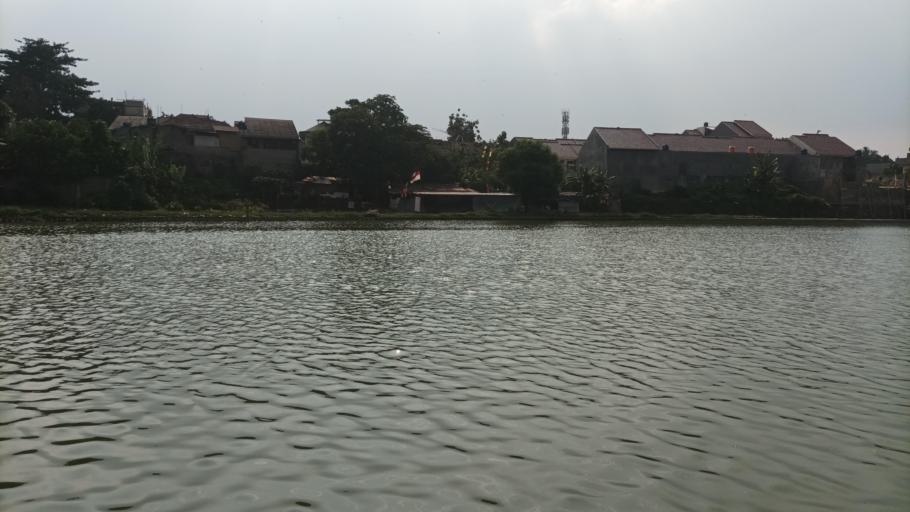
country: ID
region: West Java
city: Depok
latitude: -6.3743
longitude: 106.8687
